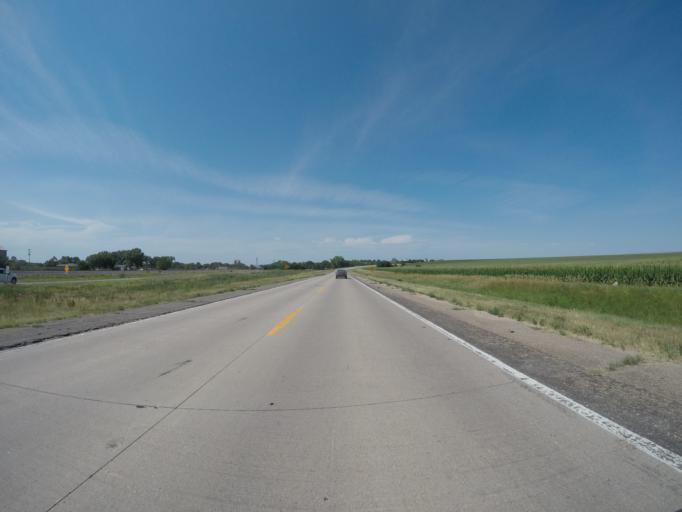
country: US
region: Nebraska
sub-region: Adams County
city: Hastings
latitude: 40.4305
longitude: -98.4383
